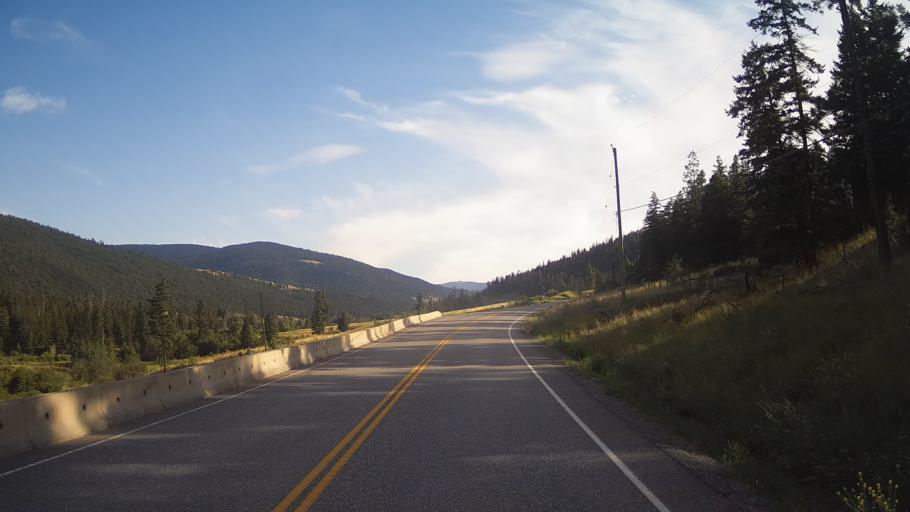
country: CA
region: British Columbia
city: Cache Creek
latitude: 50.8562
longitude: -121.5322
